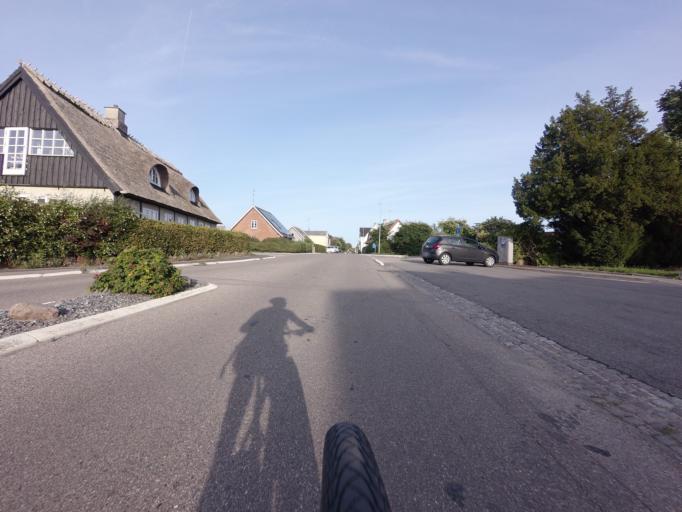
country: DK
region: Zealand
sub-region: Stevns Kommune
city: Store Heddinge
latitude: 55.2563
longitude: 12.3728
